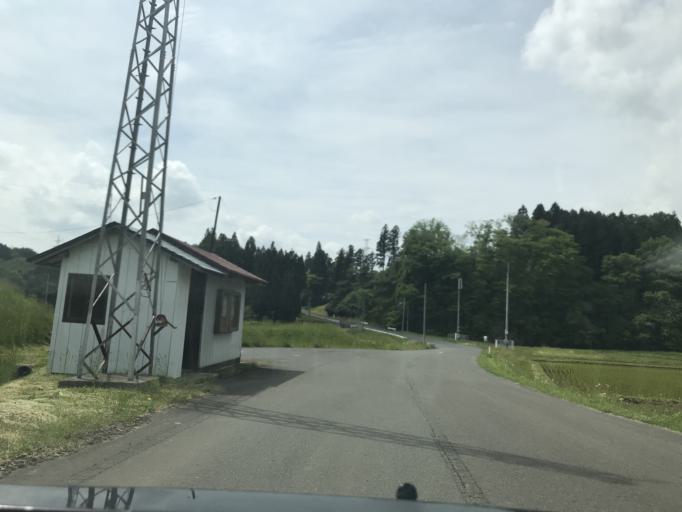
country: JP
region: Iwate
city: Ichinoseki
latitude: 38.8669
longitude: 140.9811
